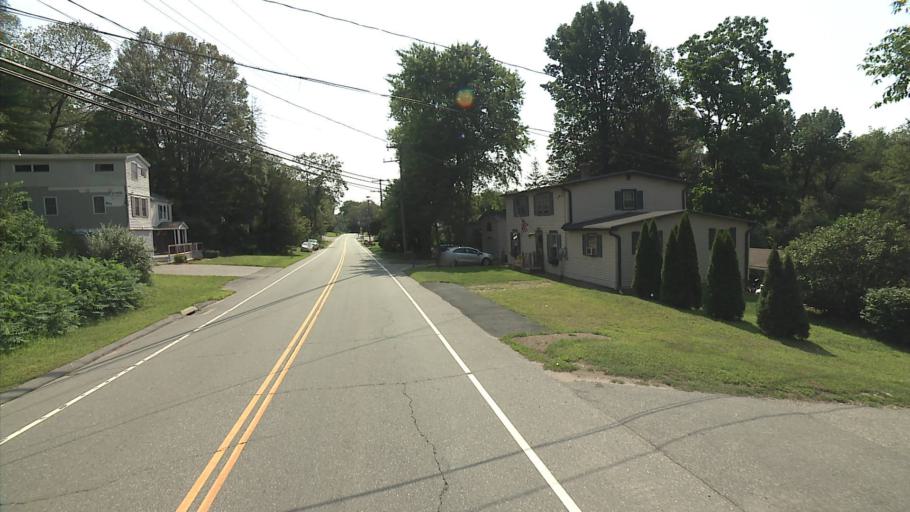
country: US
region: Connecticut
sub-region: New London County
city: Montville Center
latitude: 41.5654
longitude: -72.1668
